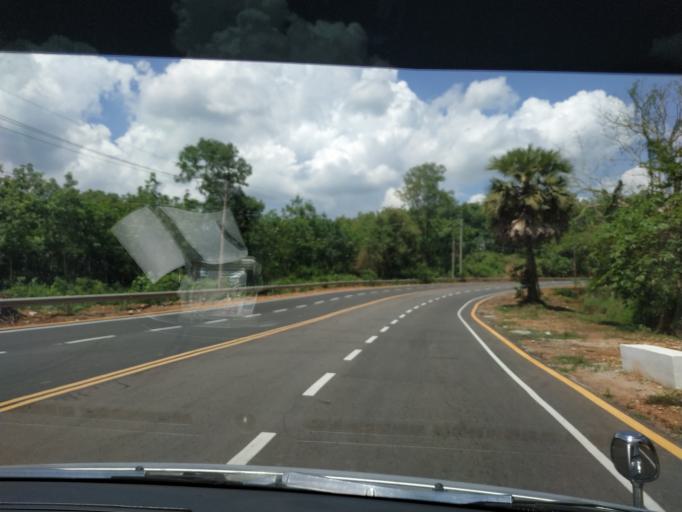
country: MM
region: Mon
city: Kyaikto
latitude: 17.3917
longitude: 97.0629
